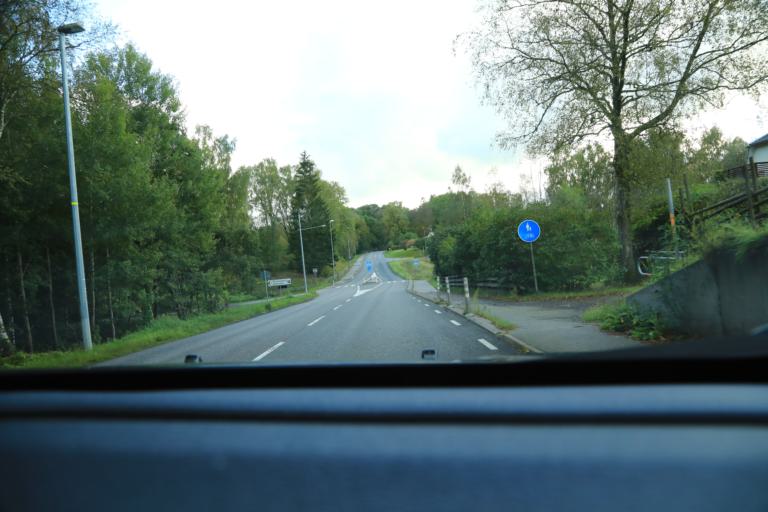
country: SE
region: Halland
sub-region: Halmstads Kommun
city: Getinge
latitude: 57.1421
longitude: 12.7256
